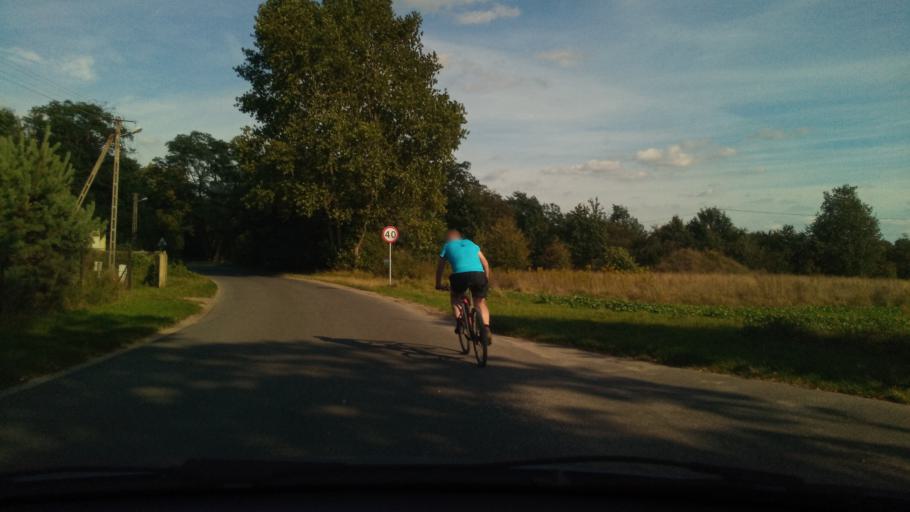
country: PL
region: Lodz Voivodeship
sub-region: Powiat piotrkowski
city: Sulejow
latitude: 51.4064
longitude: 19.8590
